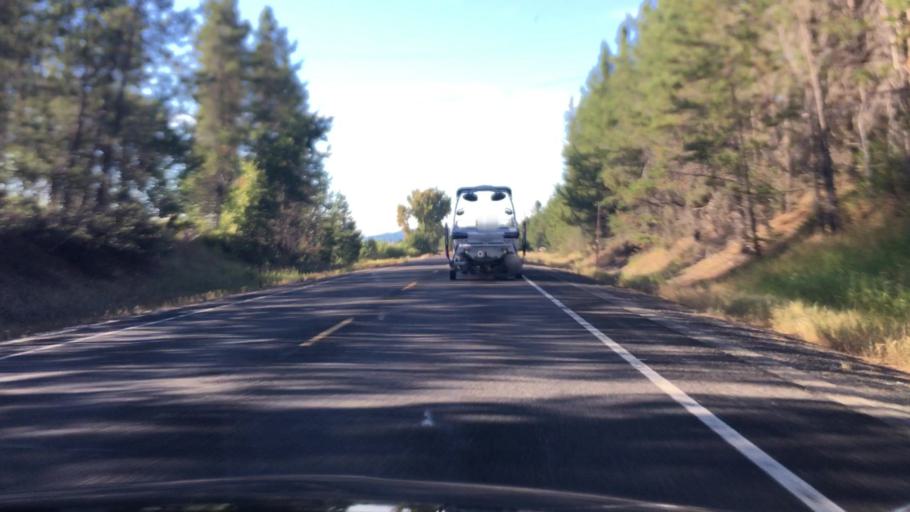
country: US
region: Idaho
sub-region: Valley County
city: Cascade
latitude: 44.4652
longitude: -115.9992
